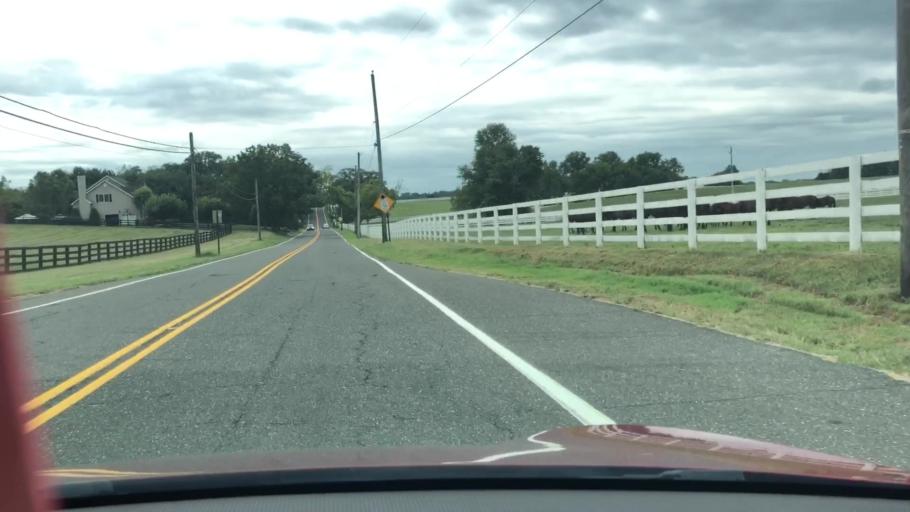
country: US
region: New Jersey
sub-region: Monmouth County
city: Shrewsbury
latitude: 40.1744
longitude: -74.5124
